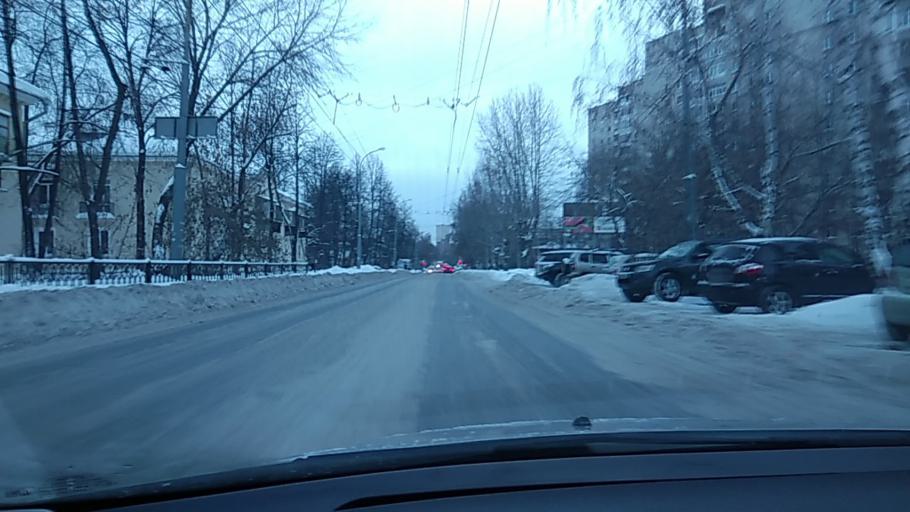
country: RU
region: Sverdlovsk
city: Yekaterinburg
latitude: 56.8987
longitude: 60.5922
